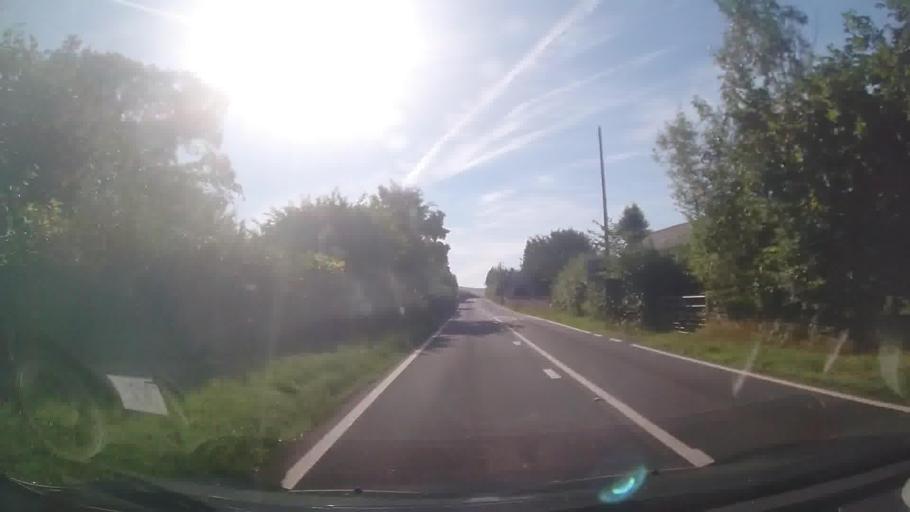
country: GB
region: Wales
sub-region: Sir Powys
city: Hay
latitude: 51.9637
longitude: -3.2066
